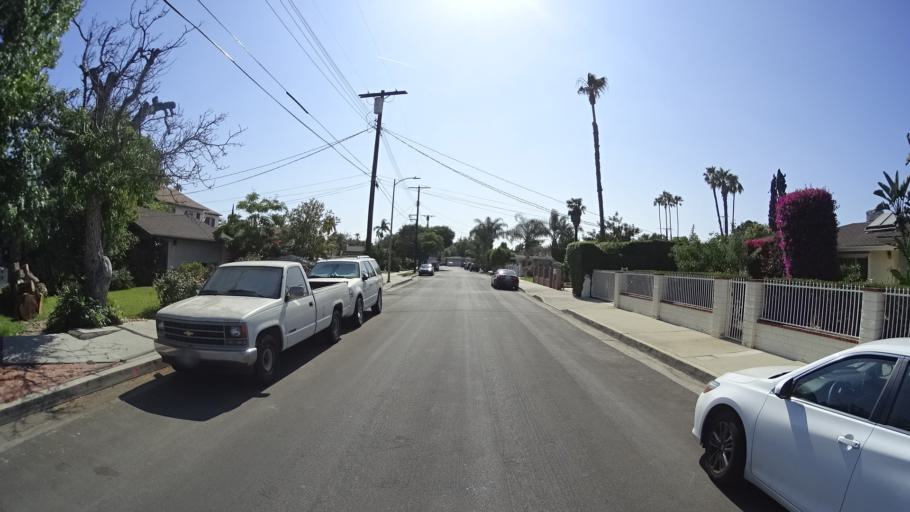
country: US
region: California
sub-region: Los Angeles County
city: Van Nuys
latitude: 34.1967
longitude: -118.4287
